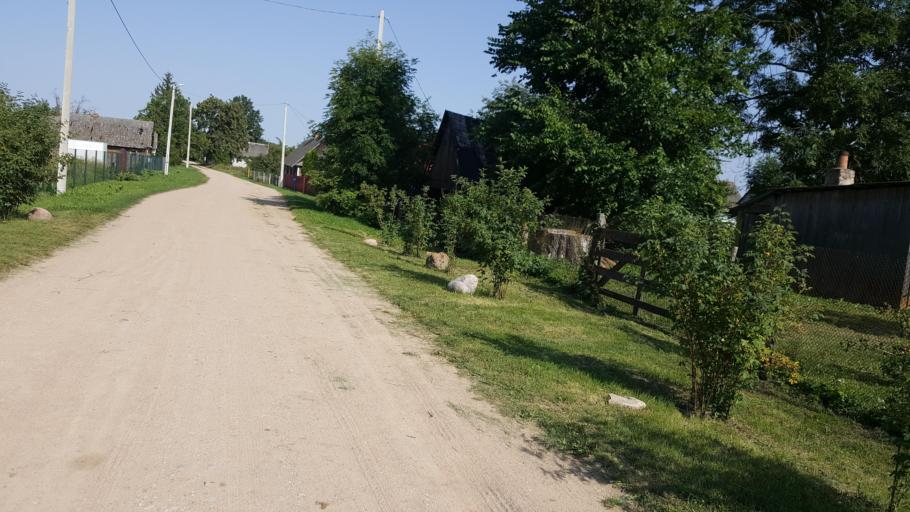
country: BY
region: Brest
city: Zhabinka
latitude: 52.2381
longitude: 24.0096
